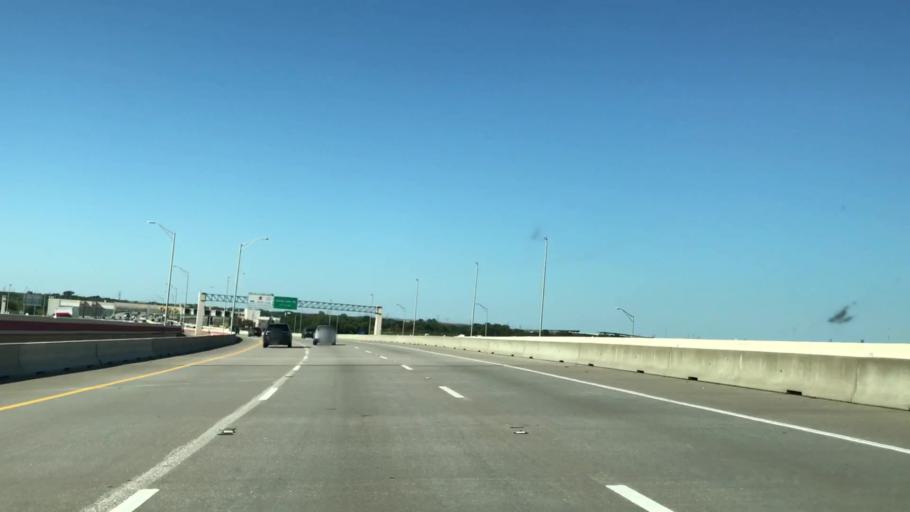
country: US
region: Texas
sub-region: Dallas County
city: Carrollton
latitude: 32.9551
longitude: -96.9261
